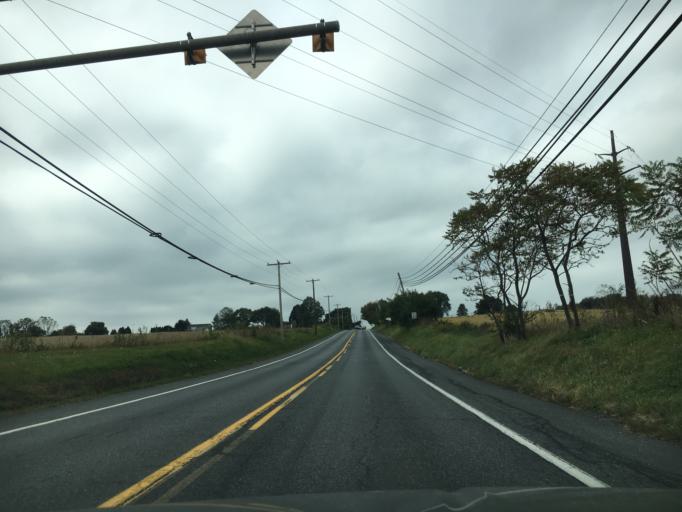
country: US
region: Pennsylvania
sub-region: Northampton County
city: North Catasauqua
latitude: 40.6978
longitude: -75.4541
